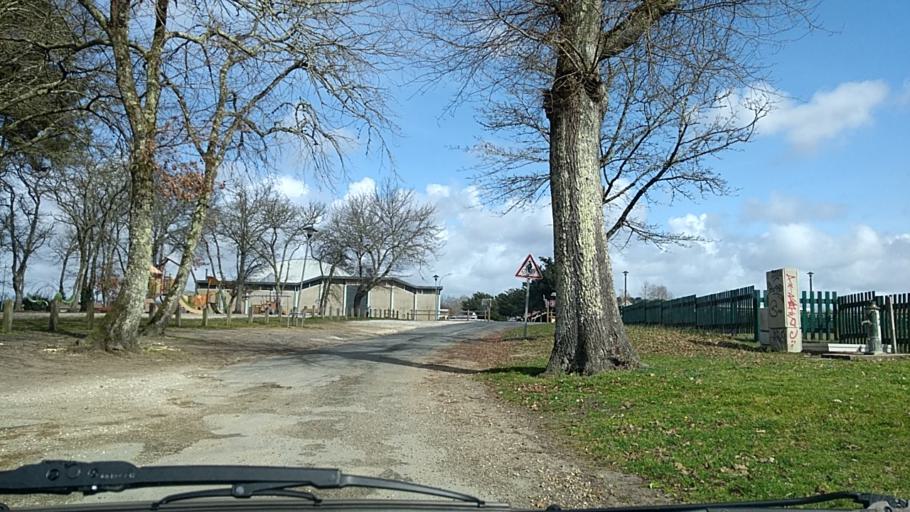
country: FR
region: Aquitaine
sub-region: Departement de la Gironde
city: Mios
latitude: 44.6049
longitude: -0.9421
